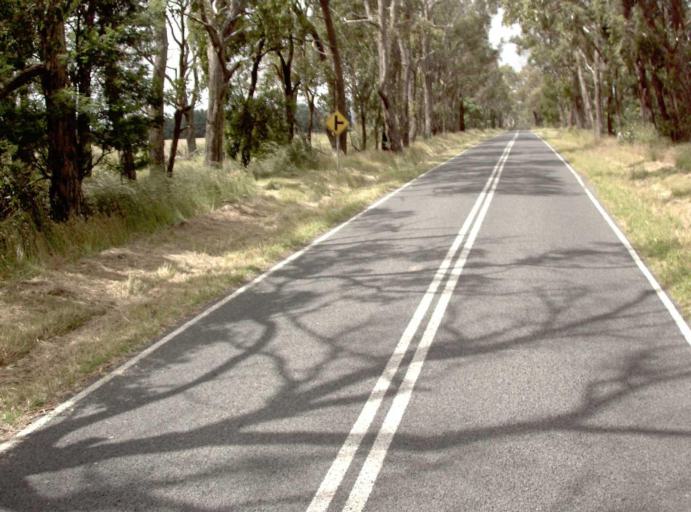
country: AU
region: Victoria
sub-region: Latrobe
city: Moe
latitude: -38.1249
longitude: 146.1483
